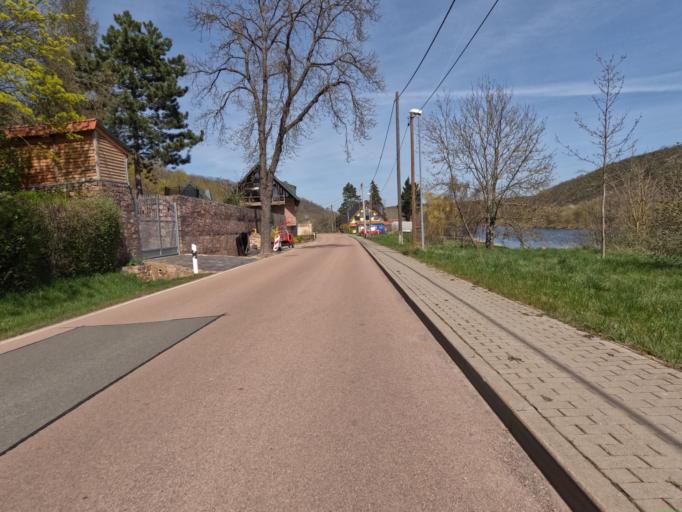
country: DE
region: Saxony-Anhalt
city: Konnern
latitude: 51.6234
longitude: 11.7482
